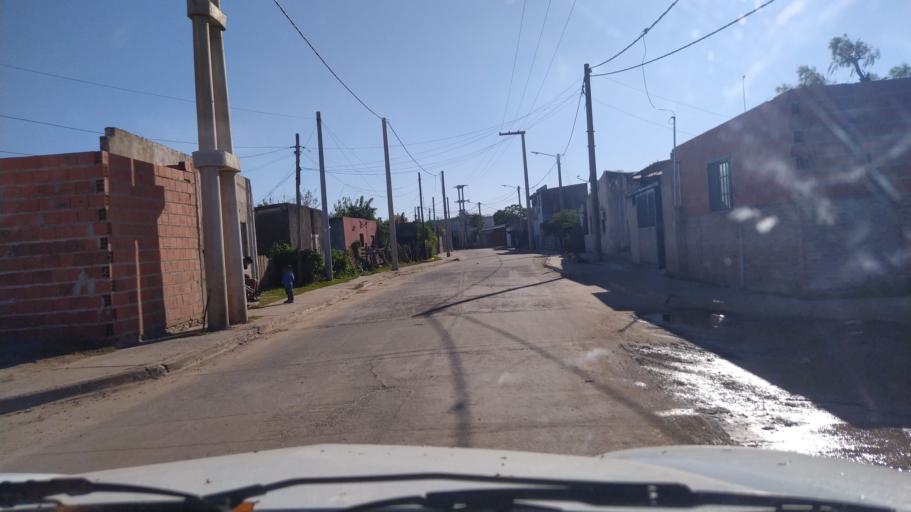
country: AR
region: Corrientes
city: Corrientes
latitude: -27.4949
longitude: -58.8074
